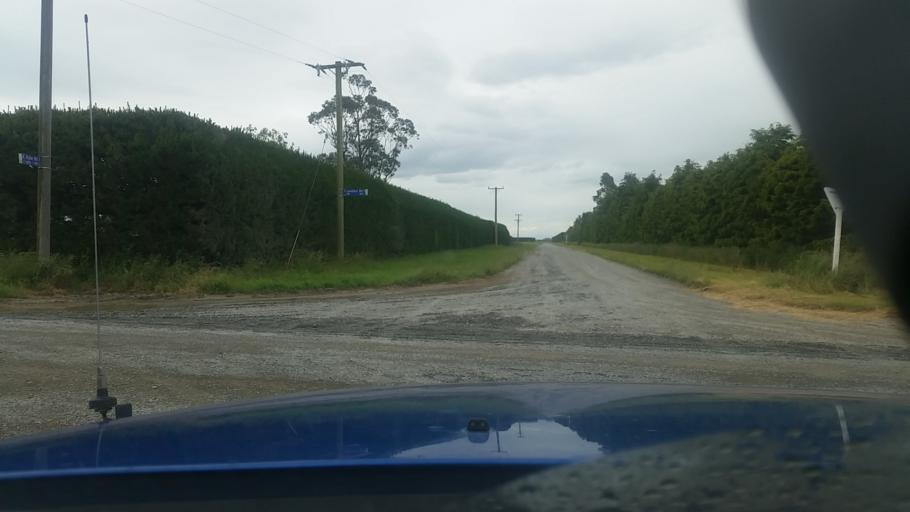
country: NZ
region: Canterbury
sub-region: Ashburton District
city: Rakaia
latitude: -43.9254
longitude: 172.0644
